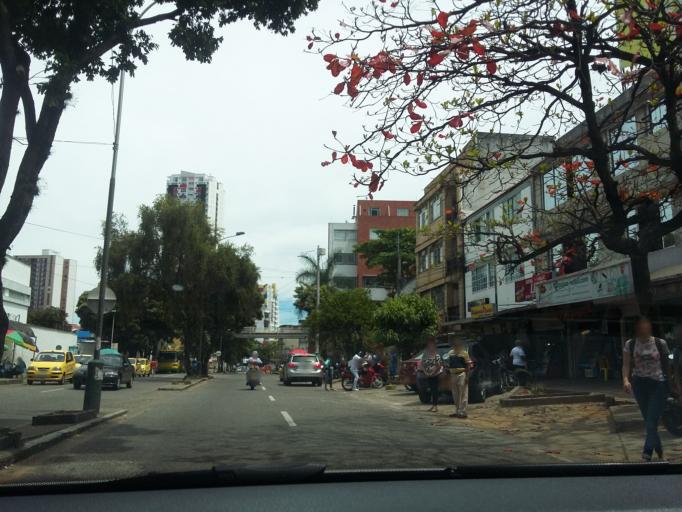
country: CO
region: Santander
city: Bucaramanga
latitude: 7.1281
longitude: -73.1133
